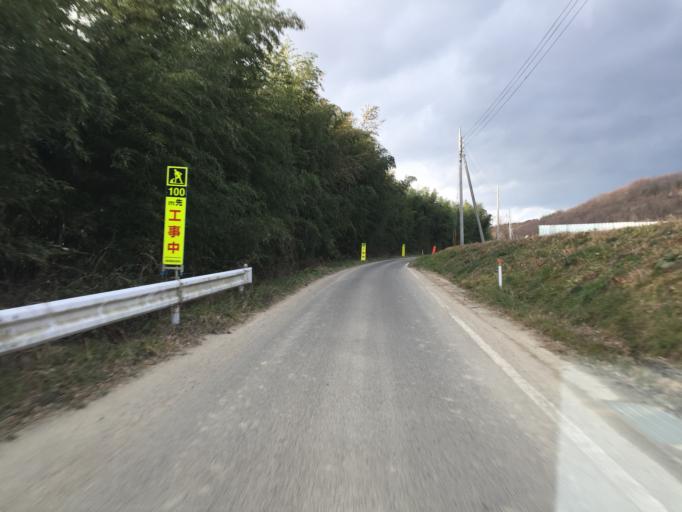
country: JP
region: Fukushima
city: Motomiya
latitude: 37.5249
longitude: 140.4151
